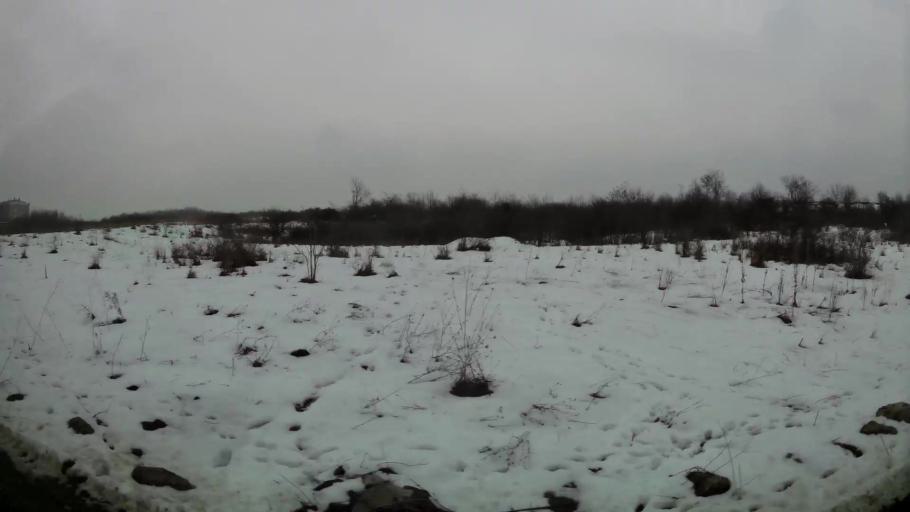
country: RS
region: Central Serbia
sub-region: Belgrade
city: Zvezdara
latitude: 44.7579
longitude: 20.5071
